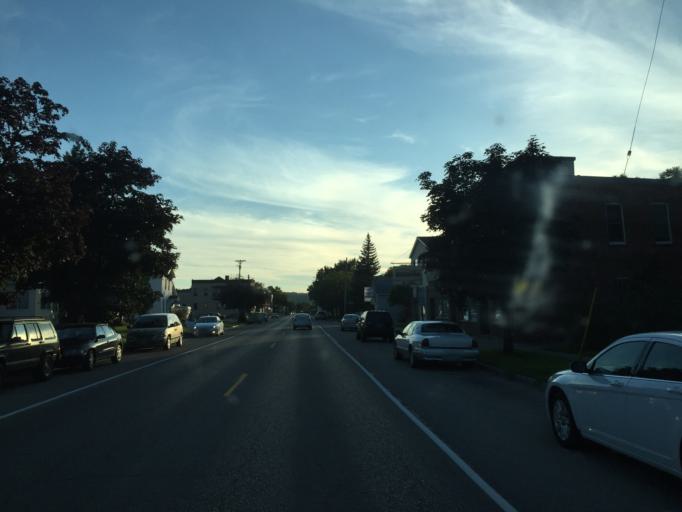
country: US
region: Minnesota
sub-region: Winona County
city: Winona
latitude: 44.0540
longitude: -91.6596
